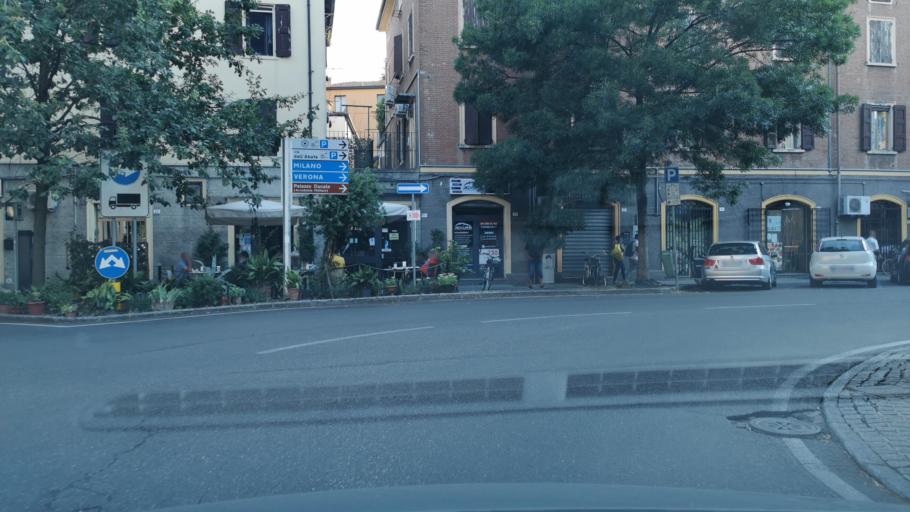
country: IT
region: Emilia-Romagna
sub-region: Provincia di Modena
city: Modena
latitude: 44.6507
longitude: 10.9360
